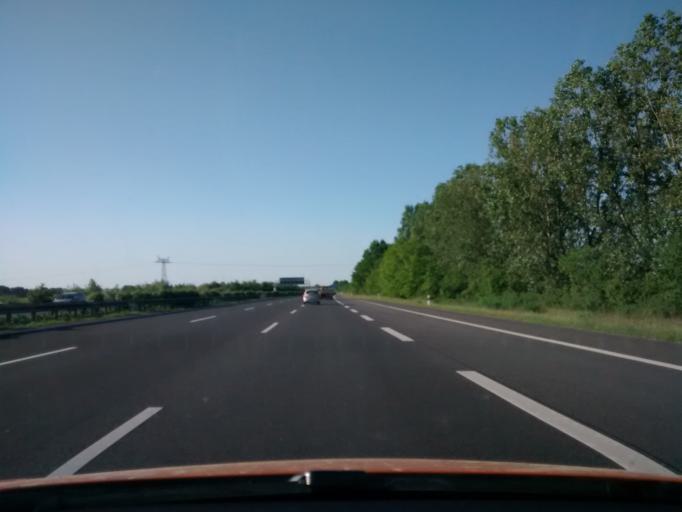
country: DE
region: Brandenburg
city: Schulzendorf
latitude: 52.3351
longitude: 13.5541
